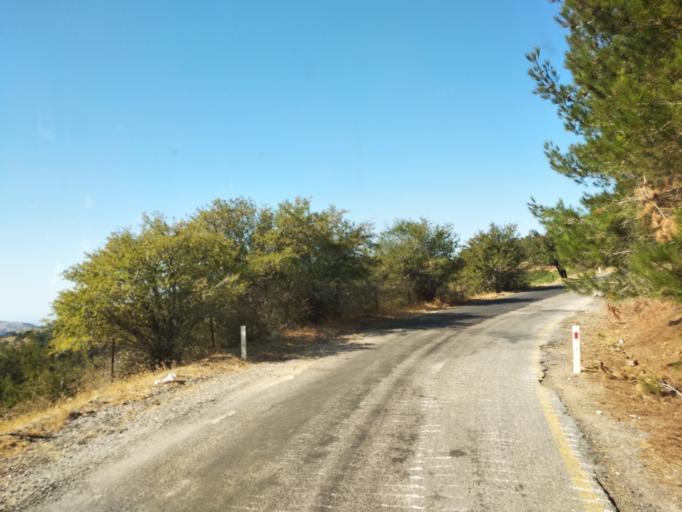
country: TR
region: Izmir
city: Gaziemir
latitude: 38.3032
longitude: 26.9974
